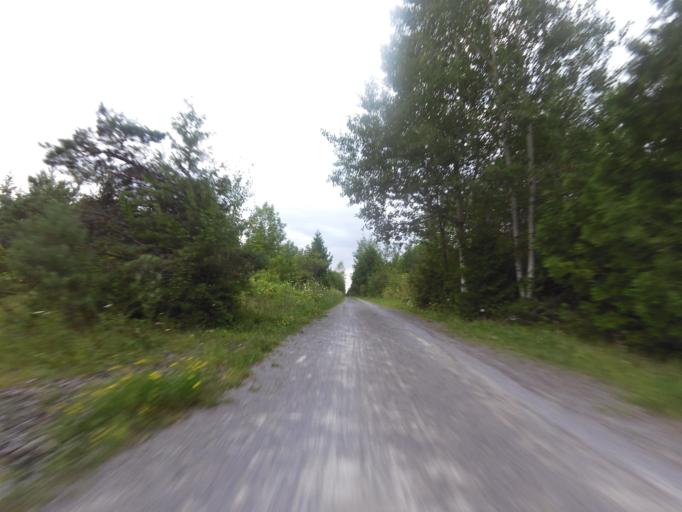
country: CA
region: Ontario
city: Carleton Place
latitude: 45.1995
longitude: -76.0139
